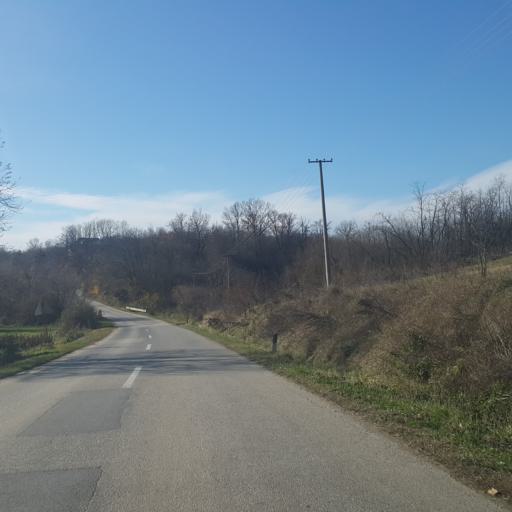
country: RS
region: Central Serbia
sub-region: Sumadijski Okrug
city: Raca
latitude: 44.2432
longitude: 20.8868
